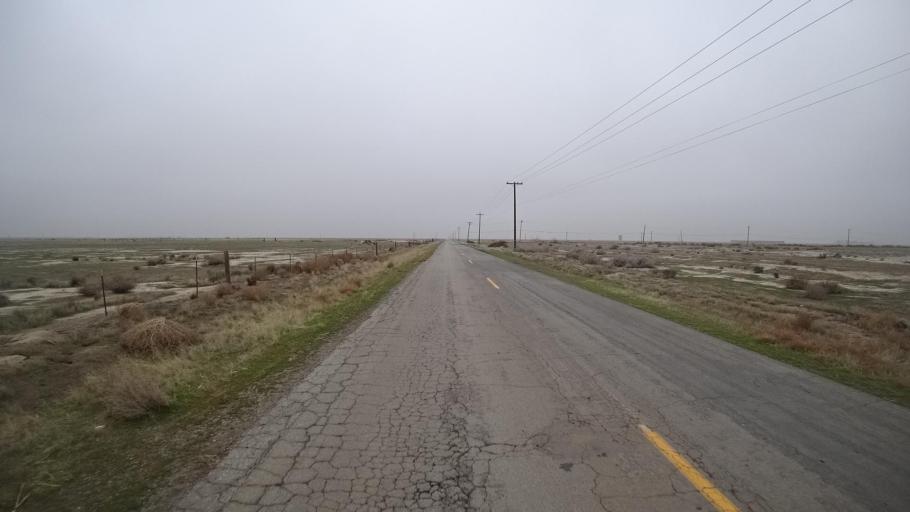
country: US
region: California
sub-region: Tulare County
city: Alpaugh
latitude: 35.7174
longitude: -119.4754
